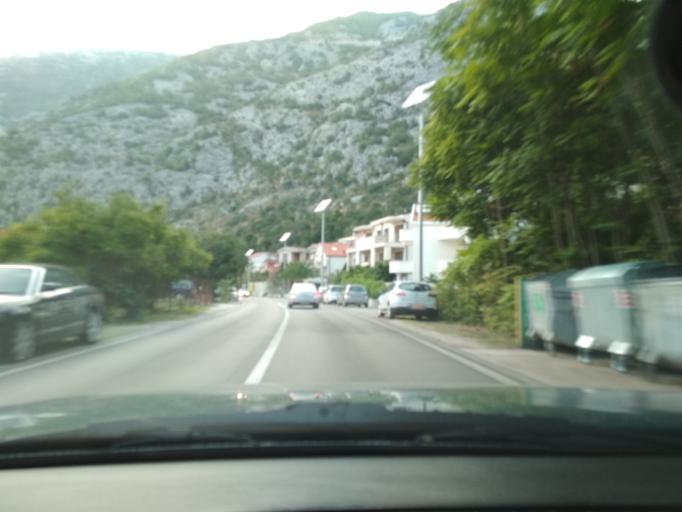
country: ME
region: Kotor
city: Risan
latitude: 42.5170
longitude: 18.6912
